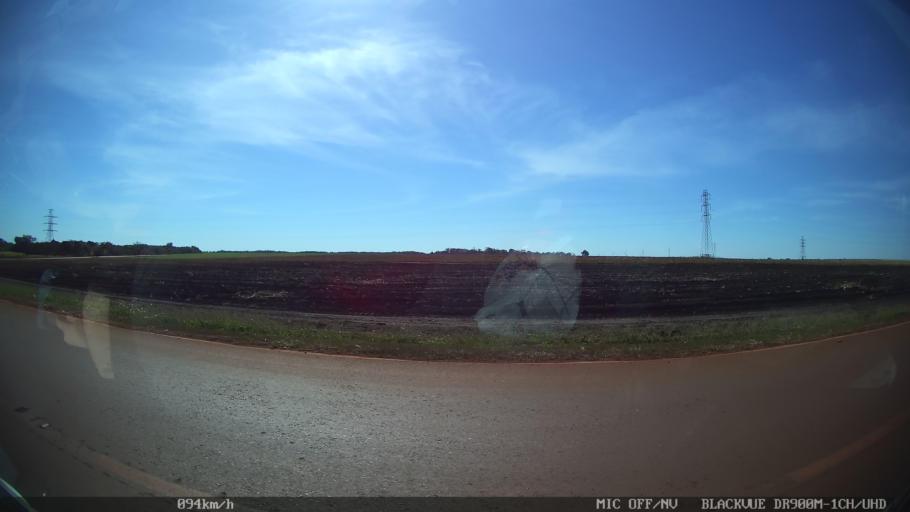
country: BR
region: Sao Paulo
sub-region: Guaira
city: Guaira
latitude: -20.4457
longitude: -48.2178
